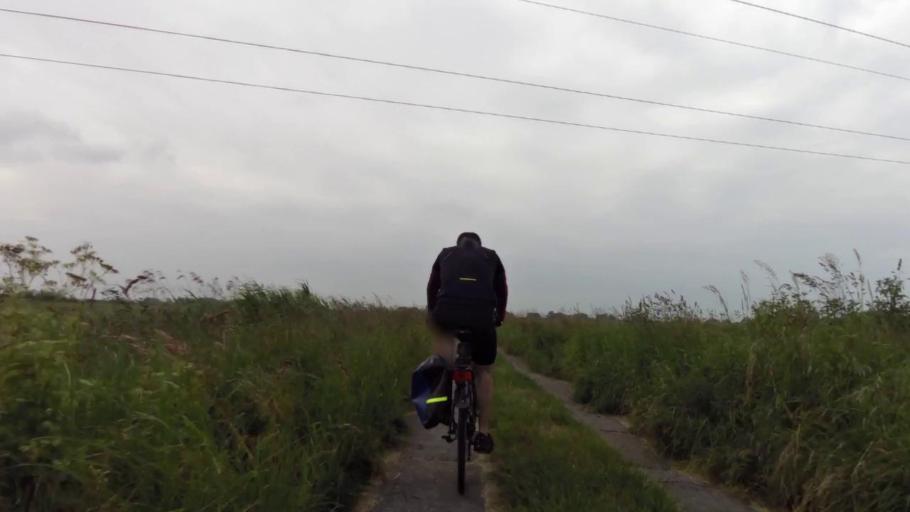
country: PL
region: West Pomeranian Voivodeship
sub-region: Powiat goleniowski
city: Stepnica
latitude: 53.5619
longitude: 14.6992
